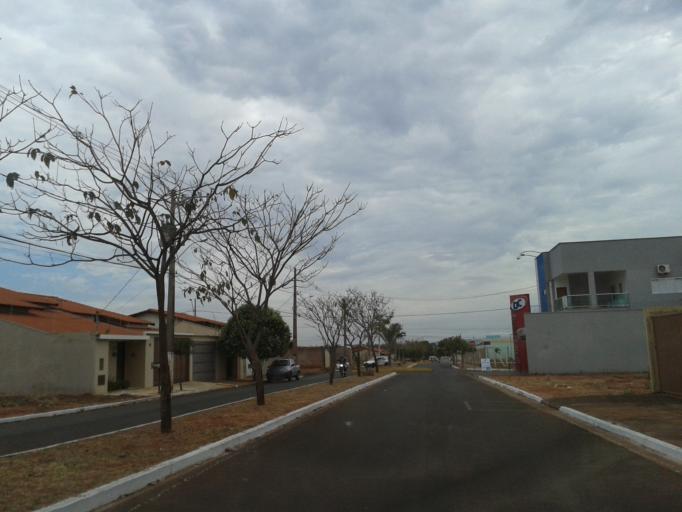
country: BR
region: Minas Gerais
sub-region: Santa Vitoria
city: Santa Vitoria
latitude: -18.8547
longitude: -50.1233
